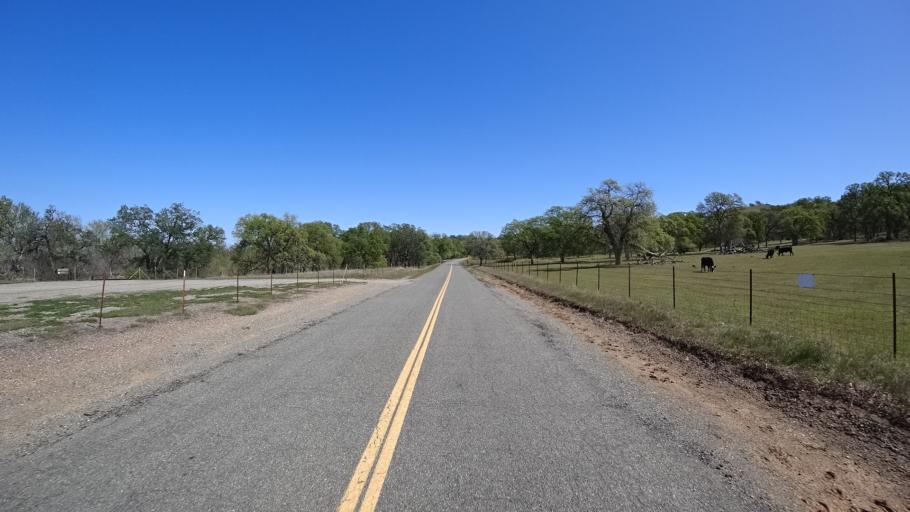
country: US
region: California
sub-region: Glenn County
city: Orland
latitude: 39.7353
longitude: -122.3975
